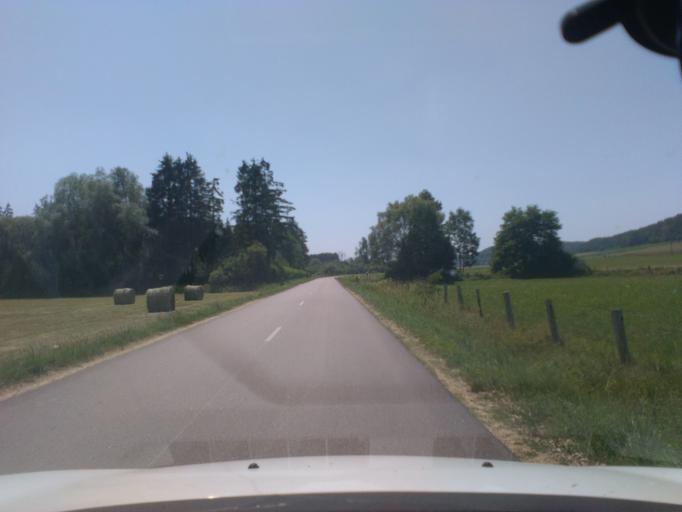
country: FR
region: Lorraine
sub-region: Departement des Vosges
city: Liffol-le-Grand
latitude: 48.3799
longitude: 5.6226
